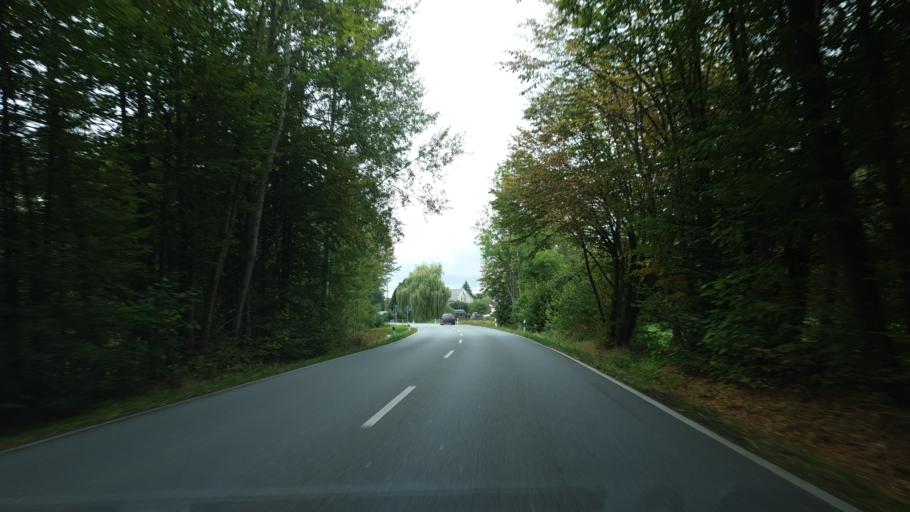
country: DE
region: Saxony
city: Glauchau
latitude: 50.8166
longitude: 12.5697
